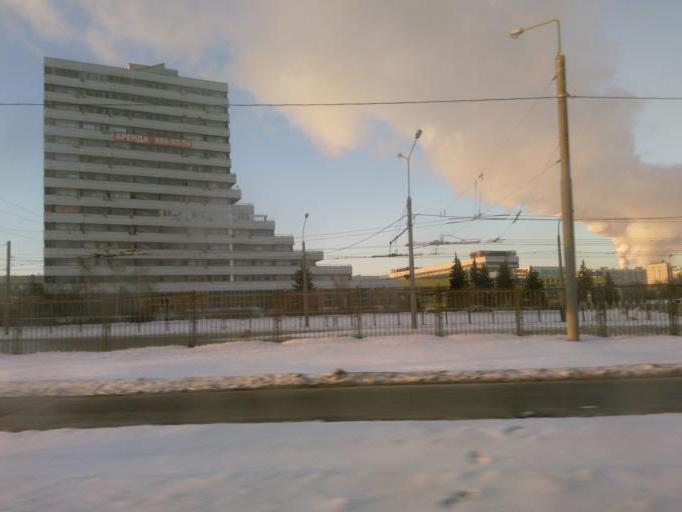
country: RU
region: Moskovskaya
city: Vostryakovo
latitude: 55.6698
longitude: 37.4474
